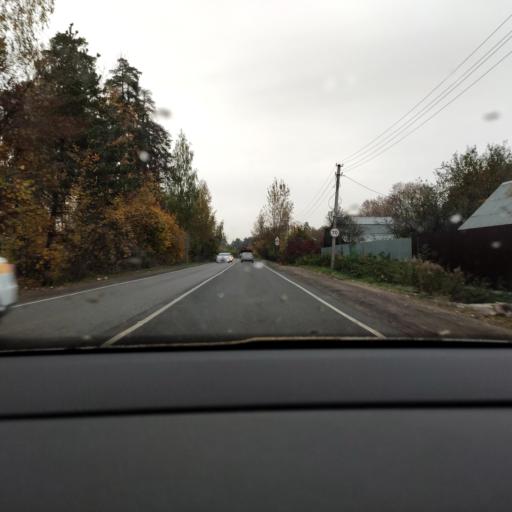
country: RU
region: Moskovskaya
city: Lesnyye Polyany
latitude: 55.9685
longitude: 37.8716
